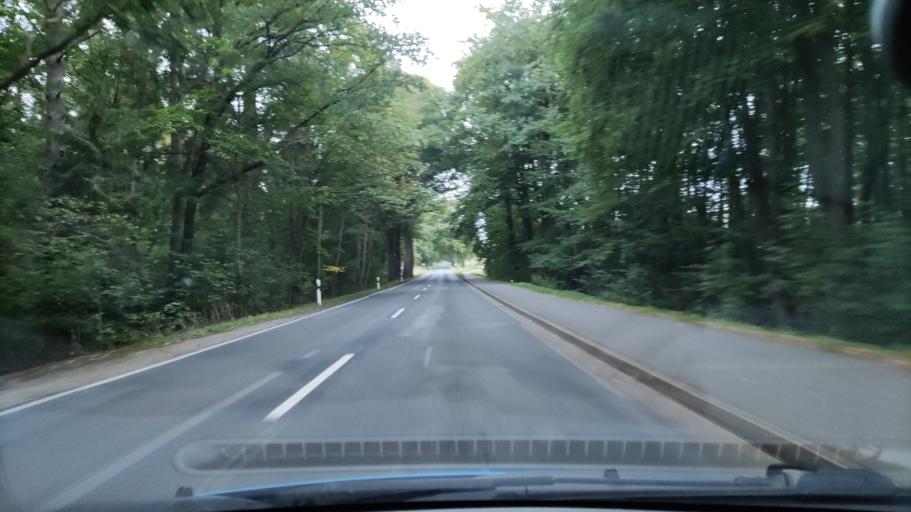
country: DE
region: Mecklenburg-Vorpommern
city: Lubtheen
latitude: 53.3849
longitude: 10.9669
